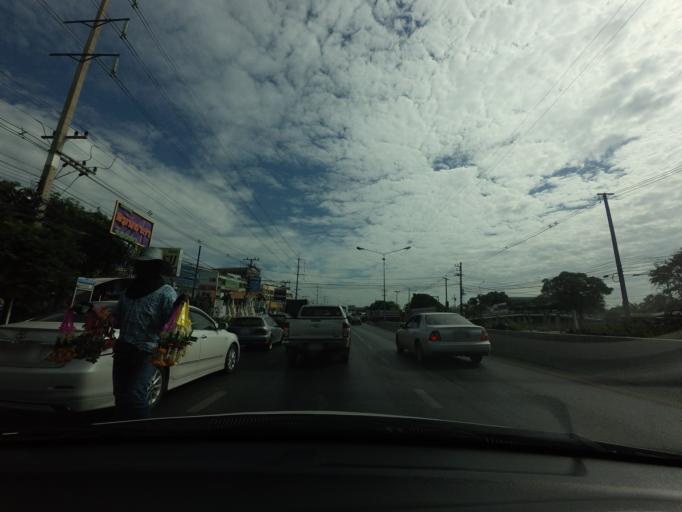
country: TH
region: Pathum Thani
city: Ban Rangsit
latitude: 14.0280
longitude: 100.7529
